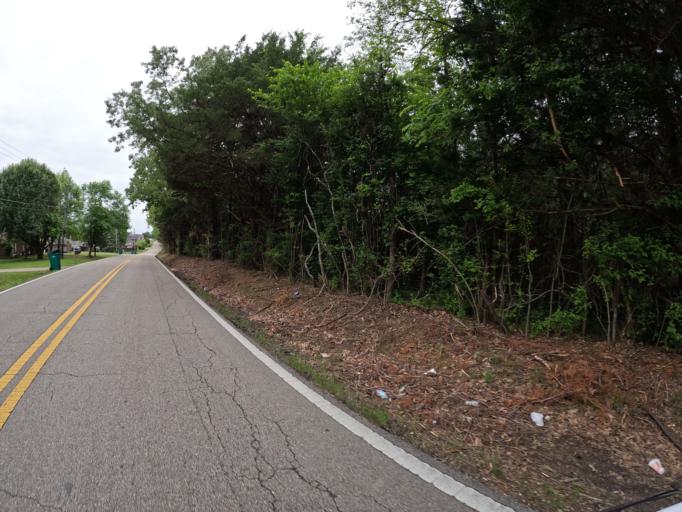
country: US
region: Mississippi
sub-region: Lee County
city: Tupelo
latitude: 34.2859
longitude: -88.7653
